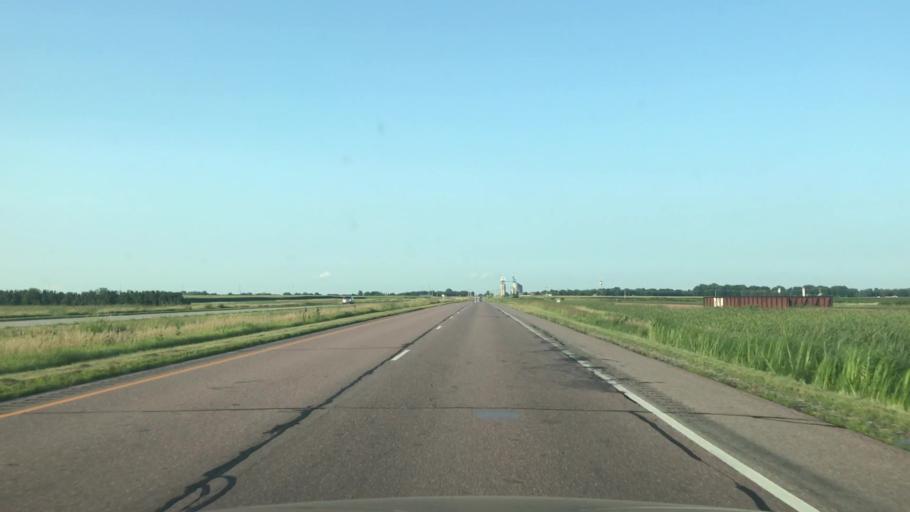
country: US
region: Minnesota
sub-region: Jackson County
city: Lakefield
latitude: 43.7816
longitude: -95.3435
